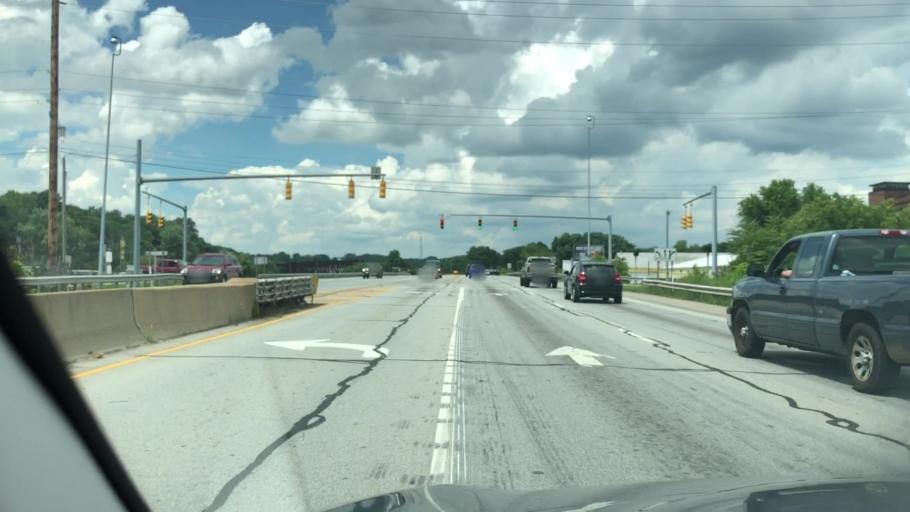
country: US
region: Ohio
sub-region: Stark County
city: Massillon
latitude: 40.7874
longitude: -81.5218
